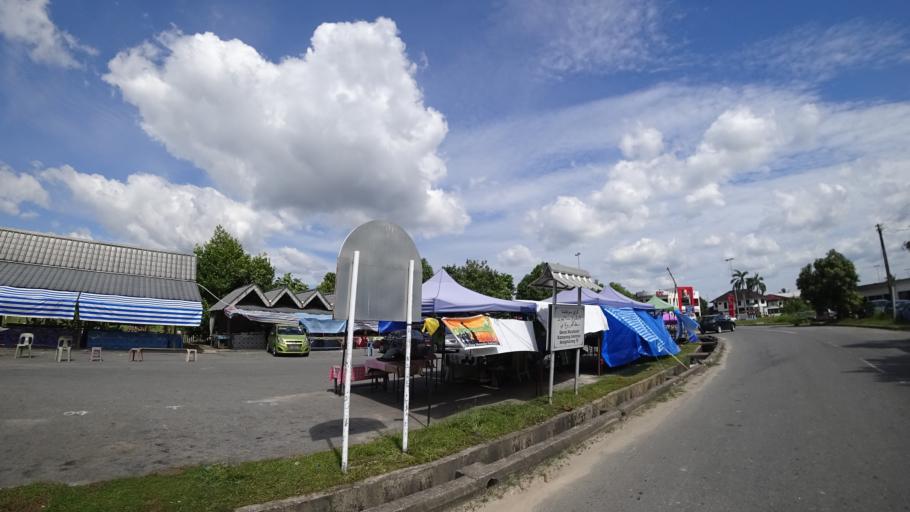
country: BN
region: Brunei and Muara
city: Bandar Seri Begawan
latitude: 4.8951
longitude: 114.8488
